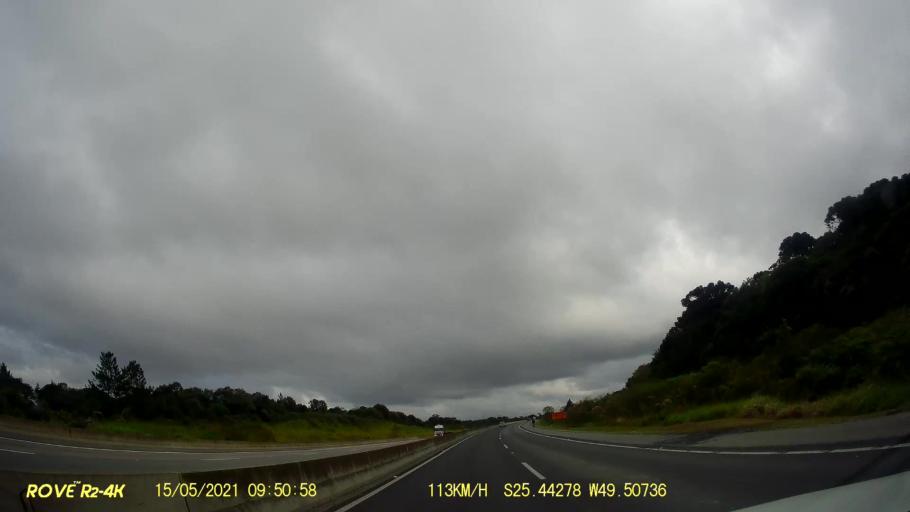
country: BR
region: Parana
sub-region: Campo Largo
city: Campo Largo
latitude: -25.4417
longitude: -49.5080
